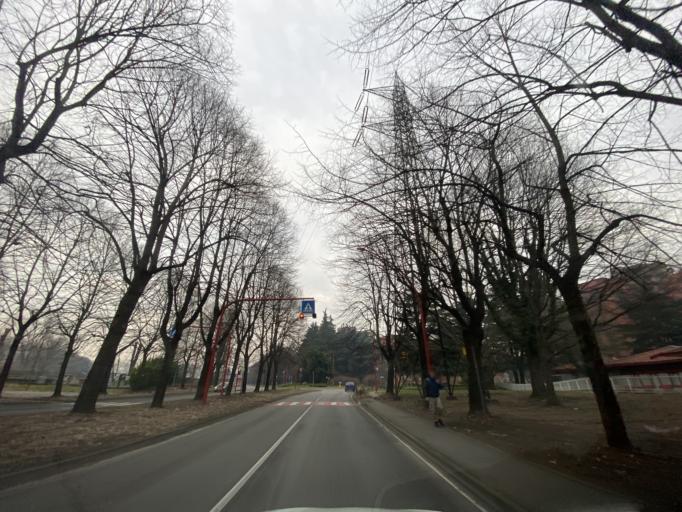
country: IT
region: Lombardy
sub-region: Citta metropolitana di Milano
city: Segrate
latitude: 45.4937
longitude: 9.2629
